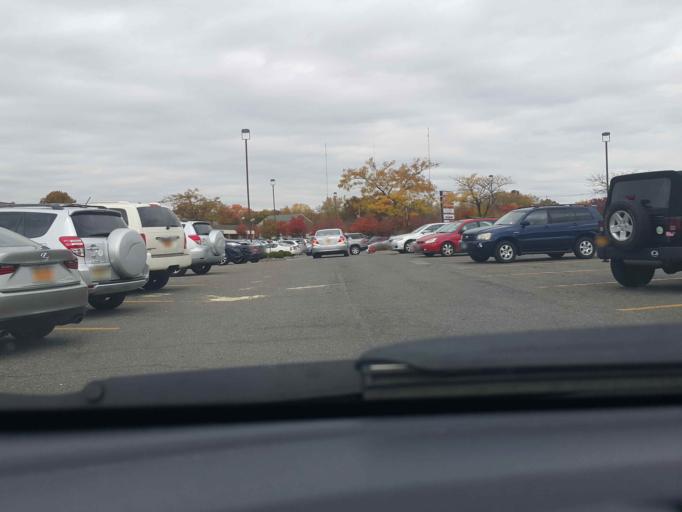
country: US
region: New York
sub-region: Rockland County
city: Nanuet
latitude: 41.0922
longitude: -74.0036
